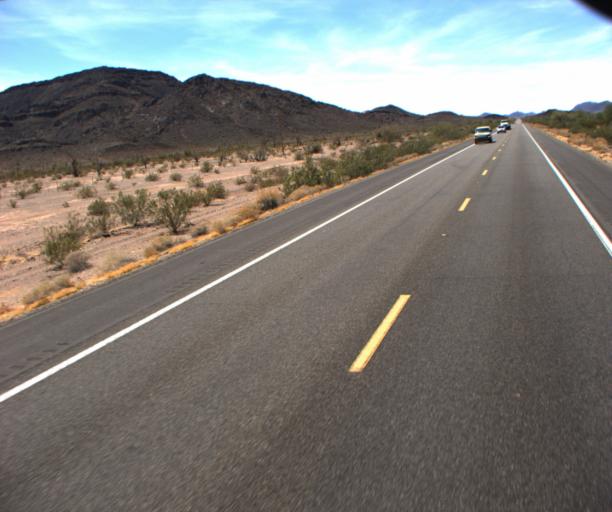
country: US
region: Arizona
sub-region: La Paz County
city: Salome
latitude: 33.6888
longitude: -113.9078
